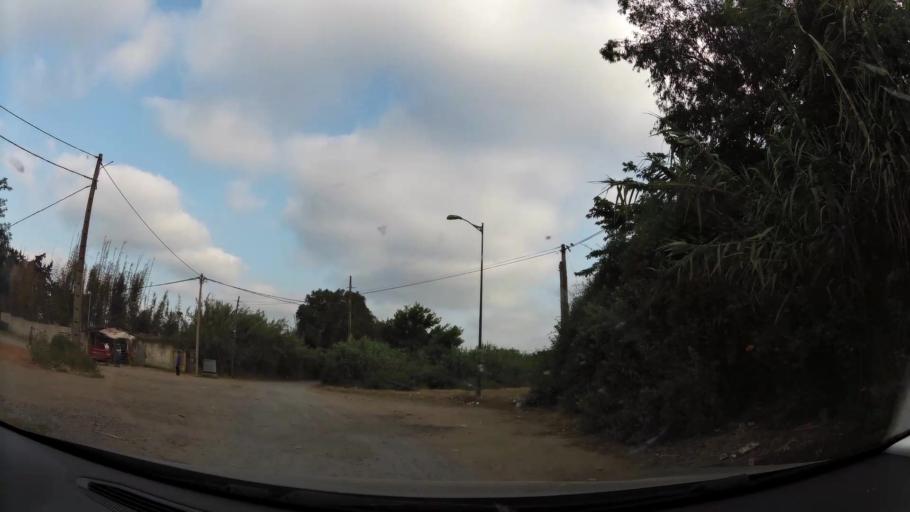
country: MA
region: Rabat-Sale-Zemmour-Zaer
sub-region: Skhirate-Temara
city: Temara
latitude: 33.9471
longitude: -6.8480
